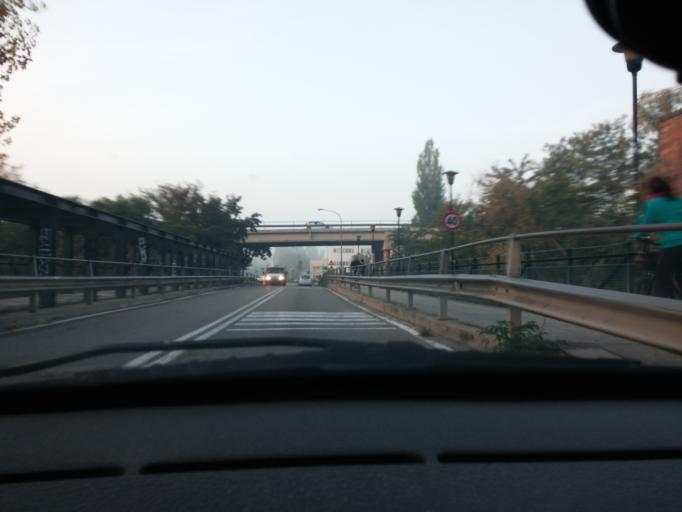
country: IT
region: Emilia-Romagna
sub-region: Provincia di Ferrara
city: Ferrara
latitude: 44.8372
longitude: 11.5998
